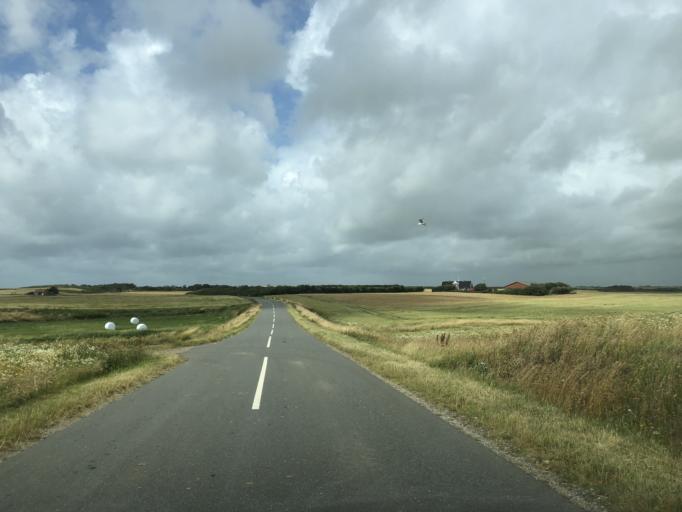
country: DK
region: Central Jutland
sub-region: Lemvig Kommune
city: Harboore
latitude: 56.4872
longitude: 8.1390
